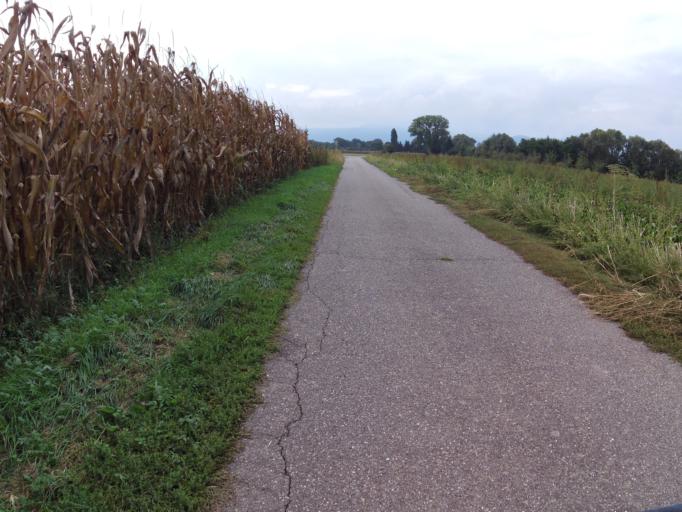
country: FR
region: Alsace
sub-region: Departement du Haut-Rhin
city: Guemar
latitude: 48.1864
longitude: 7.4070
